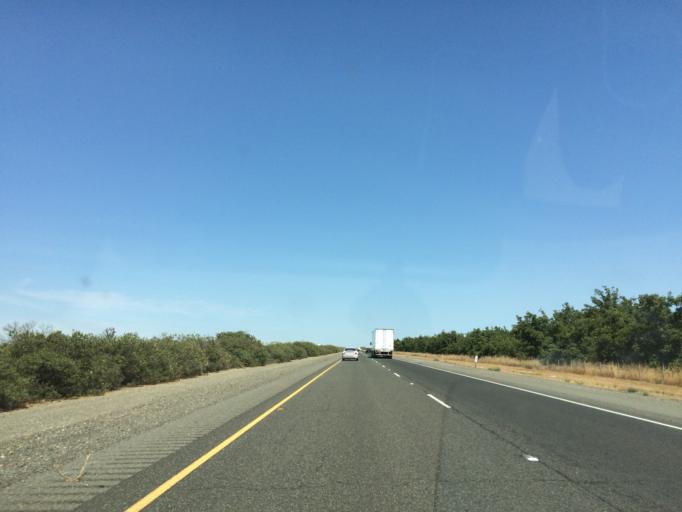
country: US
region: California
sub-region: Glenn County
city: Orland
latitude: 39.6411
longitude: -122.2043
